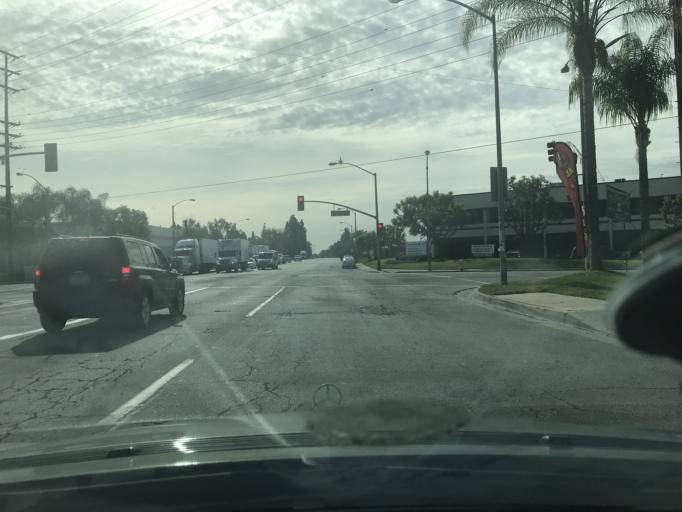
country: US
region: California
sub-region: Los Angeles County
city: Santa Fe Springs
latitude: 33.9579
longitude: -118.0715
